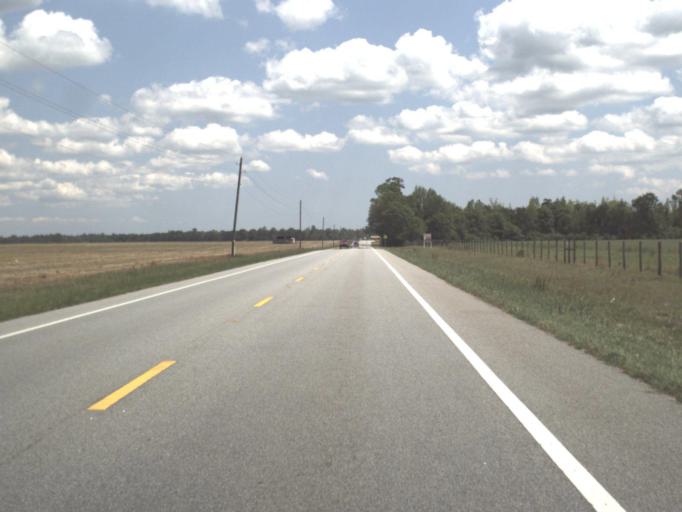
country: US
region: Florida
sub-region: Escambia County
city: Molino
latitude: 30.7464
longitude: -87.3692
